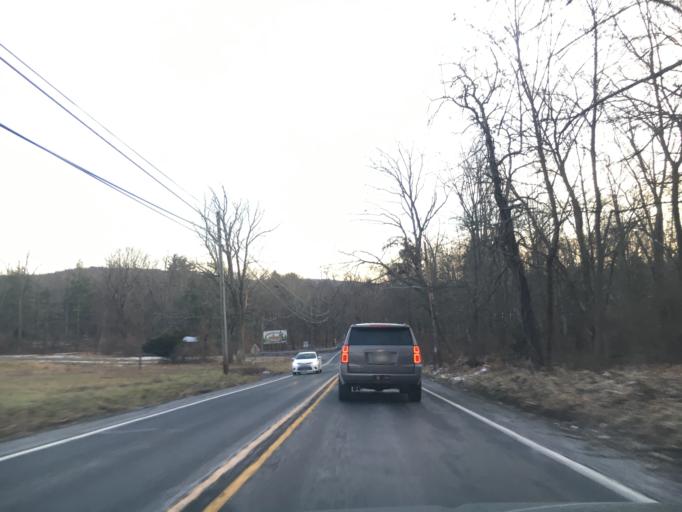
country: US
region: Pennsylvania
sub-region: Monroe County
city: East Stroudsburg
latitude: 41.0463
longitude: -75.1280
